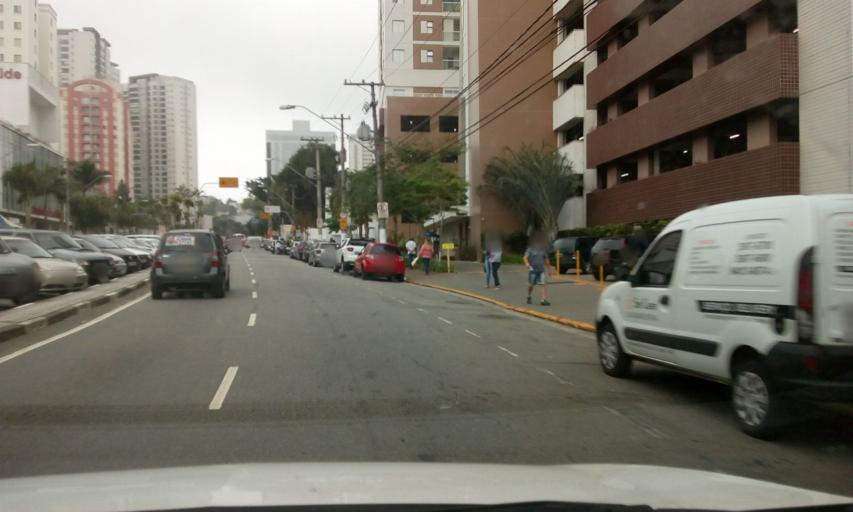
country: BR
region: Sao Paulo
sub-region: Sao Bernardo Do Campo
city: Sao Bernardo do Campo
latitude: -23.6979
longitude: -46.5486
